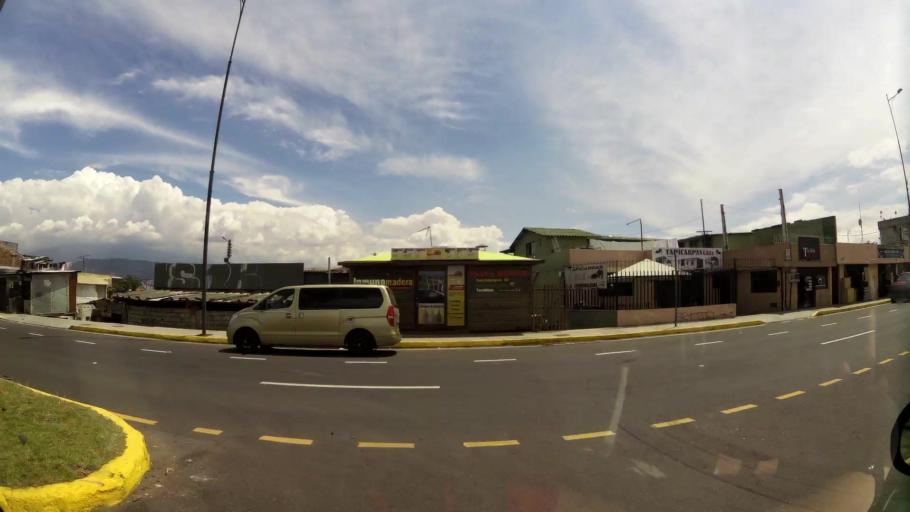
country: EC
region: Pichincha
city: Quito
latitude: -0.2037
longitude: -78.3770
